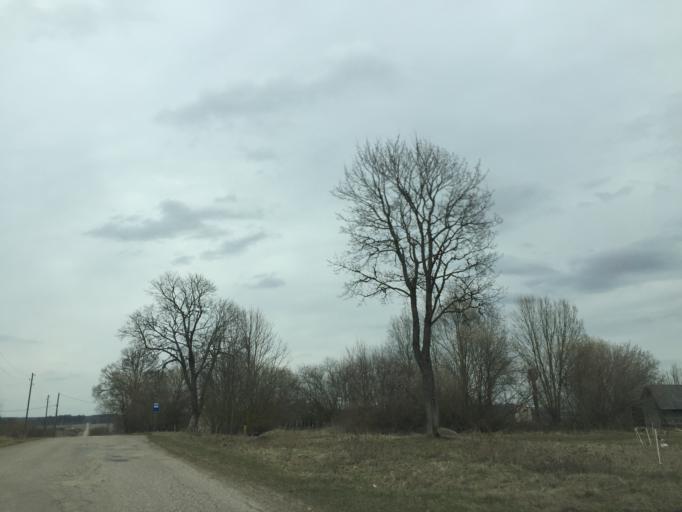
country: LV
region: Ilukste
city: Ilukste
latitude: 56.0196
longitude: 26.2727
